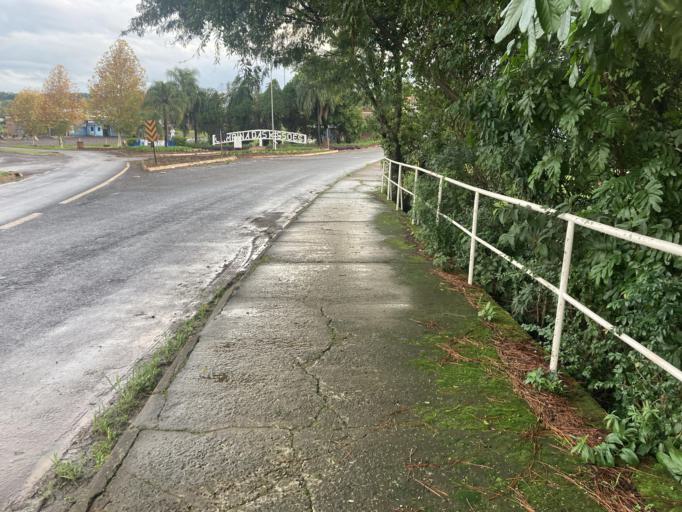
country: BR
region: Rio Grande do Sul
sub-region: Sao Pedro Do Butia
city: Butia Inferior
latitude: -27.9895
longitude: -54.8320
